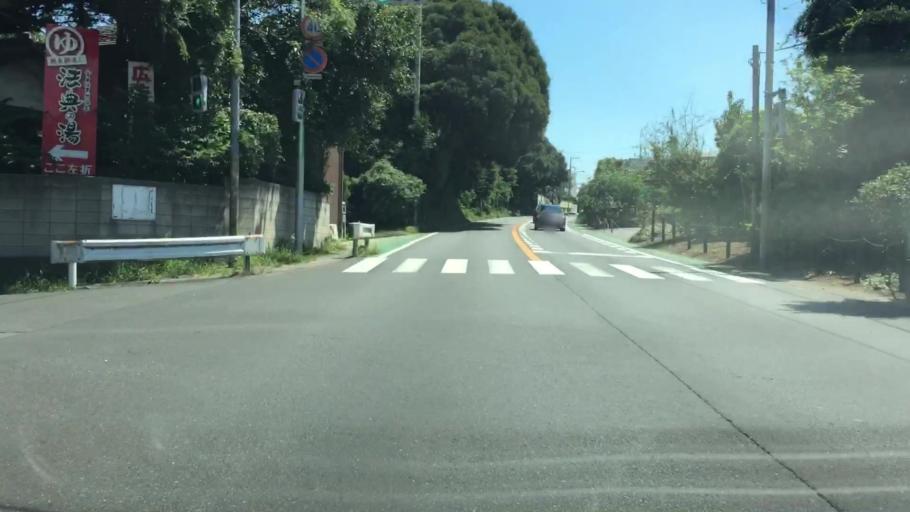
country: JP
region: Chiba
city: Funabashi
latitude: 35.7343
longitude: 139.9585
